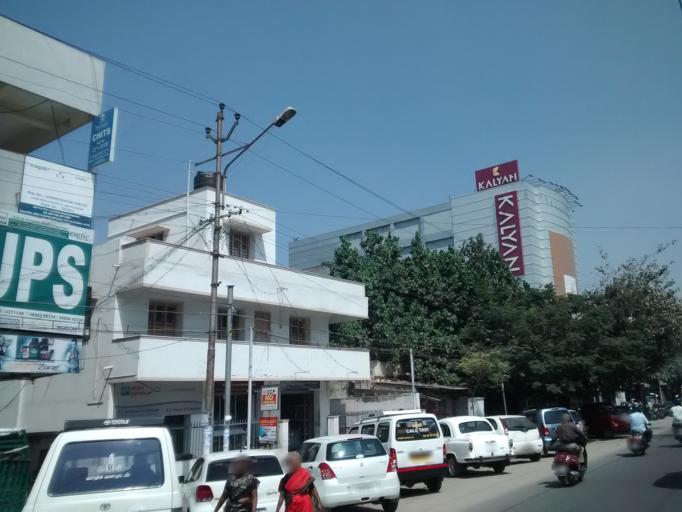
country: IN
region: Tamil Nadu
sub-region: Coimbatore
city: Coimbatore
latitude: 11.0200
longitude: 76.9664
